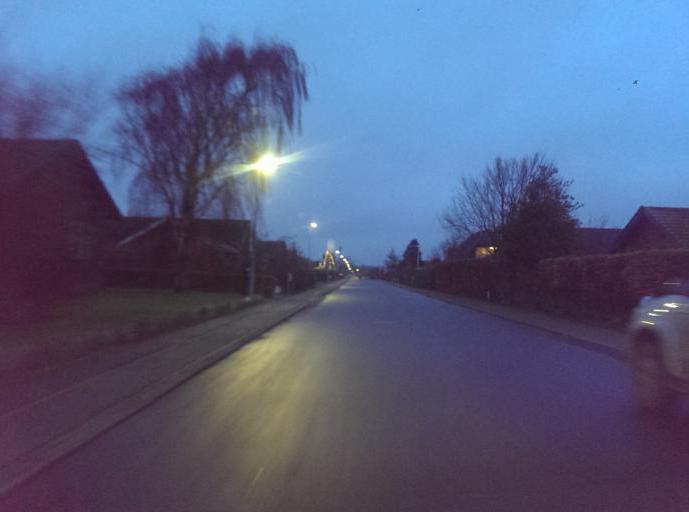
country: DK
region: South Denmark
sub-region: Esbjerg Kommune
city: Tjaereborg
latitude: 55.4993
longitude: 8.5337
